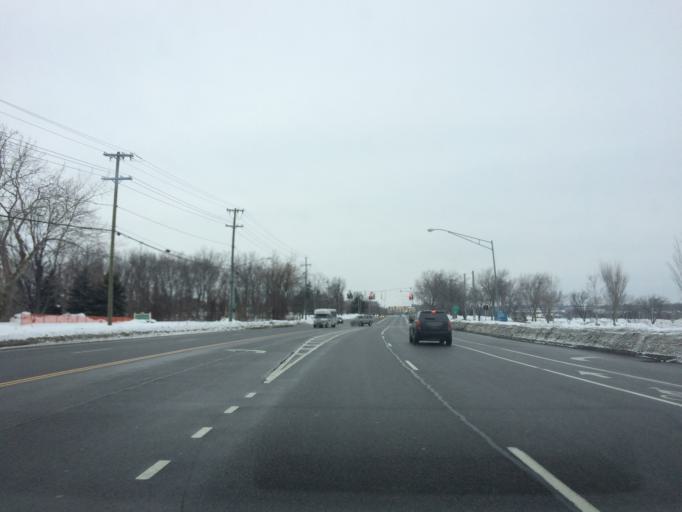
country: US
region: New York
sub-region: Monroe County
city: Rochester
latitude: 43.0972
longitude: -77.6129
